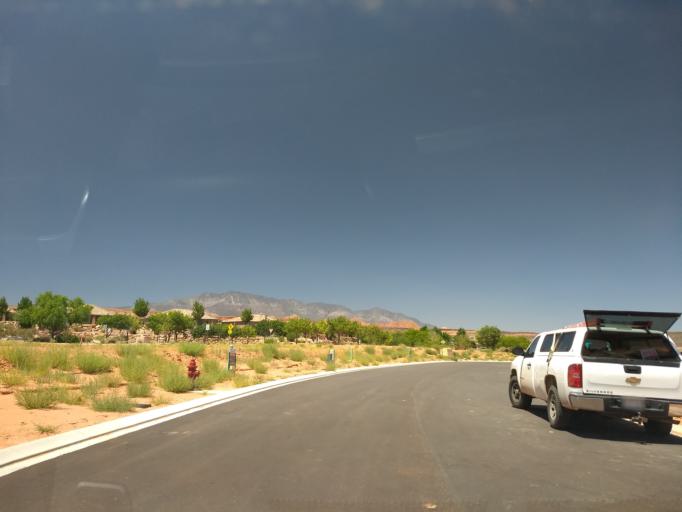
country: US
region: Utah
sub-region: Washington County
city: Washington
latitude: 37.1366
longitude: -113.4832
